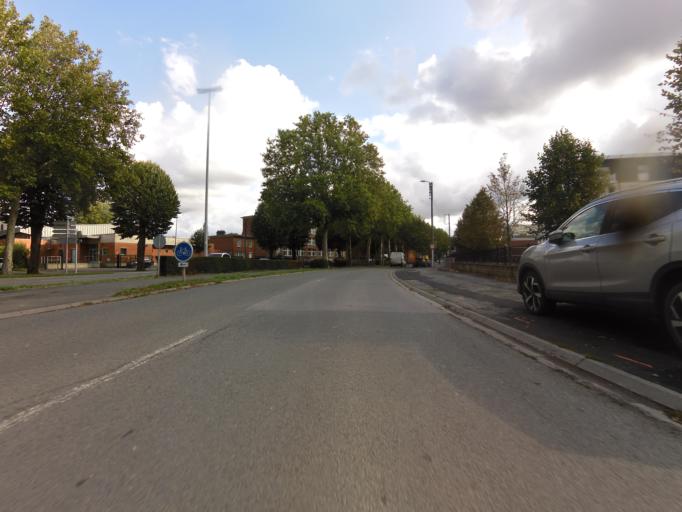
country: FR
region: Nord-Pas-de-Calais
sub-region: Departement du Nord
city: Neuville-Saint-Remy
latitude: 50.1739
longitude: 3.2232
